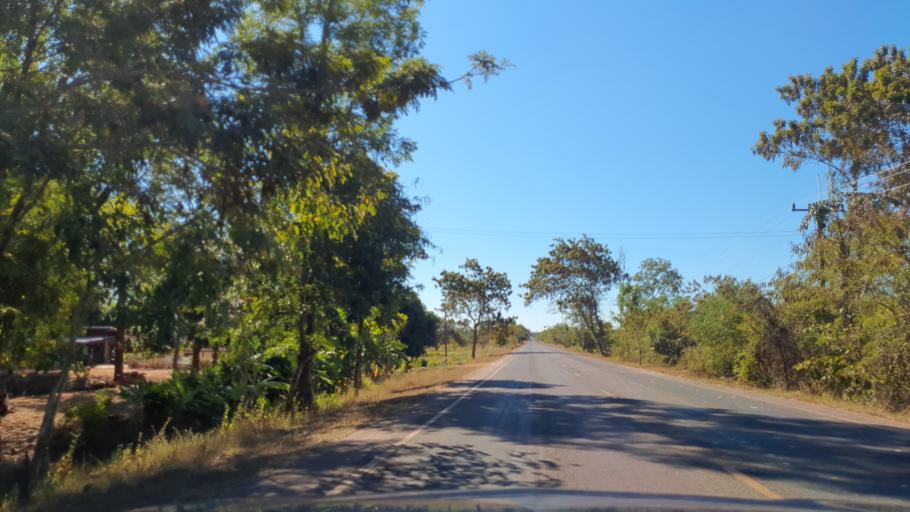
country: TH
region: Nakhon Phanom
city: Si Songkhram
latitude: 17.7478
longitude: 104.2862
